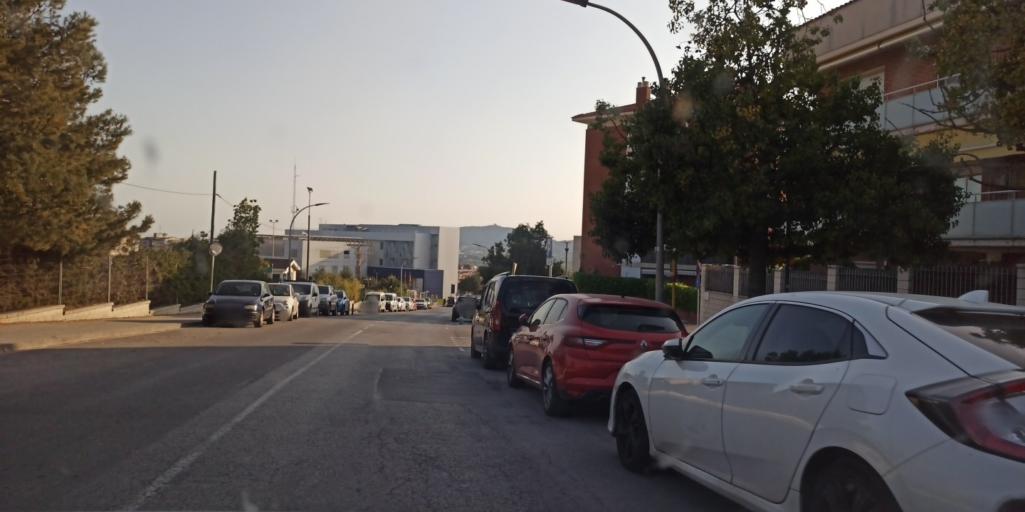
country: ES
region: Catalonia
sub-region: Provincia de Barcelona
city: Sant Feliu de Llobregat
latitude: 41.3918
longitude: 2.0494
